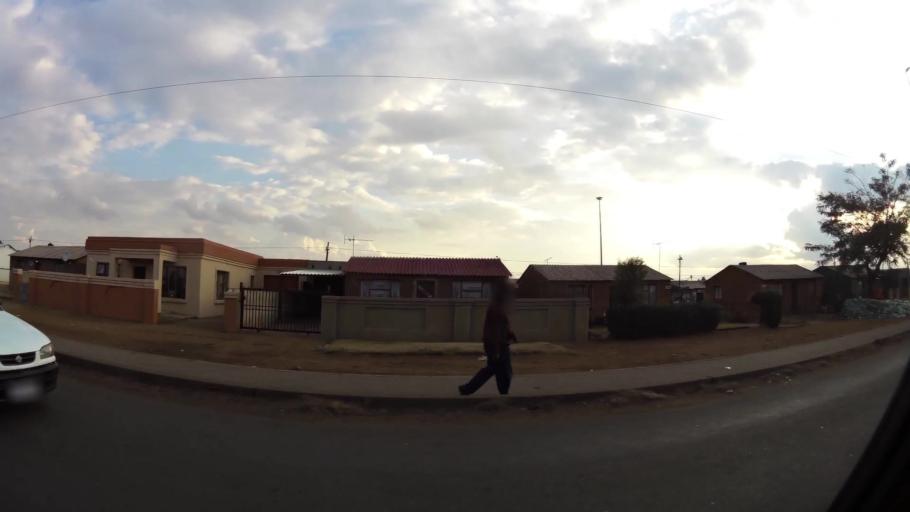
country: ZA
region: Gauteng
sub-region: City of Johannesburg Metropolitan Municipality
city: Orange Farm
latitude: -26.5809
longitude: 27.8426
